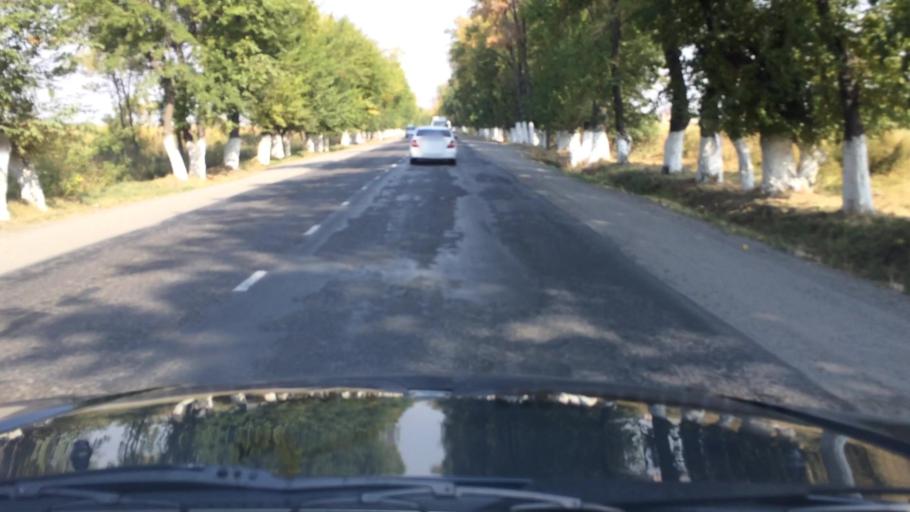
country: KG
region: Chuy
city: Lebedinovka
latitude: 42.9057
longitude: 74.6864
